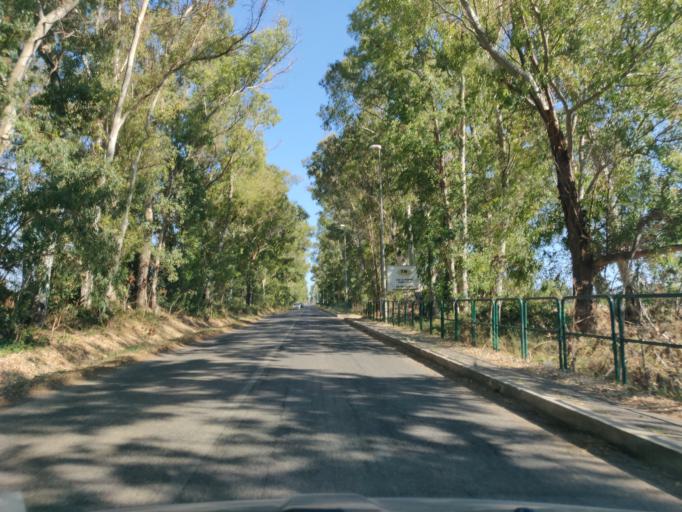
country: IT
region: Latium
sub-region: Citta metropolitana di Roma Capitale
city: Aurelia
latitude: 42.1433
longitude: 11.7641
